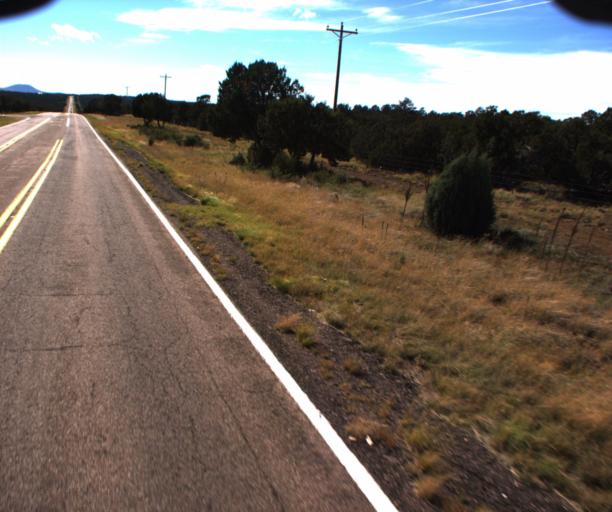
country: US
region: Arizona
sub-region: Navajo County
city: White Mountain Lake
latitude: 34.3065
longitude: -109.7789
